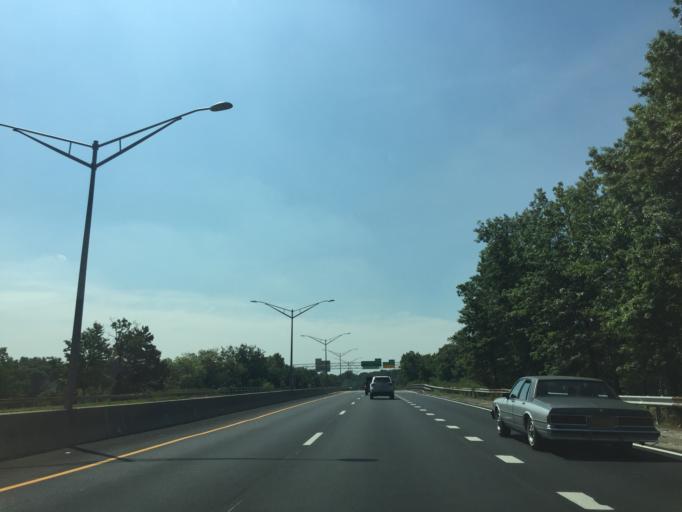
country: US
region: New York
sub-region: Nassau County
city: Bellerose Terrace
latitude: 40.7388
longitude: -73.7691
